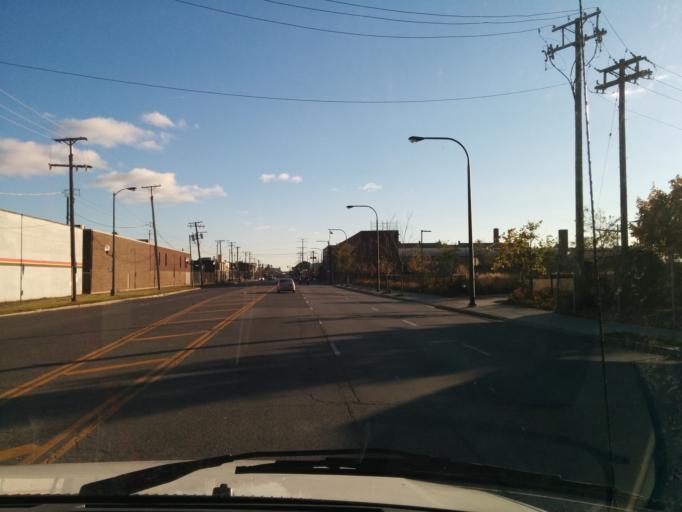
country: US
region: Illinois
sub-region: Cook County
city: Chicago
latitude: 41.8515
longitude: -87.6661
